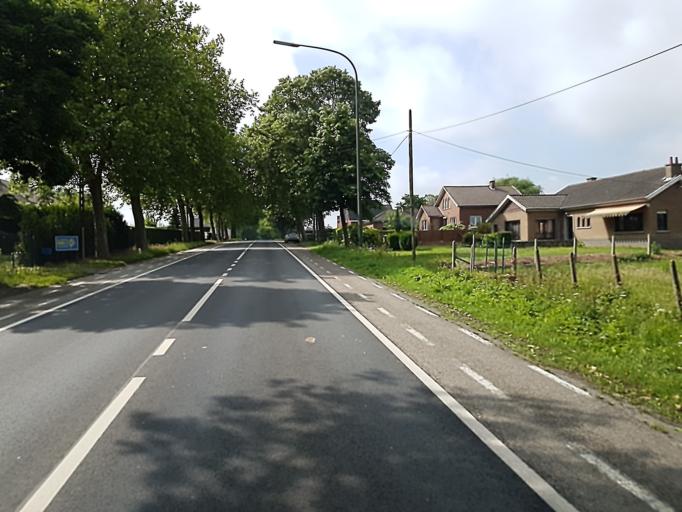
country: BE
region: Wallonia
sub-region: Province du Hainaut
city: Soignies
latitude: 50.6095
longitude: 4.0570
